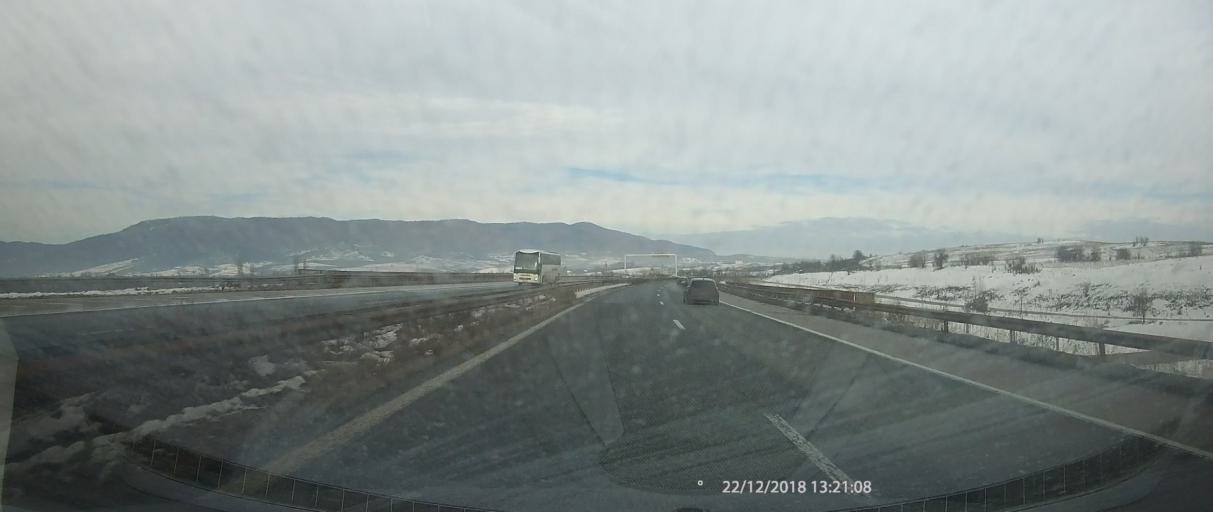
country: BG
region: Lovech
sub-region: Obshtina Yablanitsa
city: Yablanitsa
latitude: 42.9705
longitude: 24.0343
